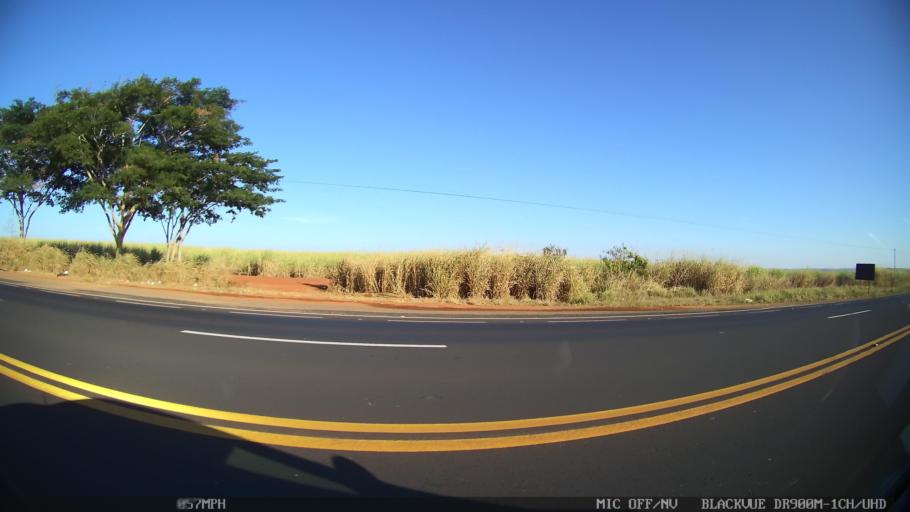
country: BR
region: Sao Paulo
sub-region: Guapiacu
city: Guapiacu
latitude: -20.7361
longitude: -49.0776
